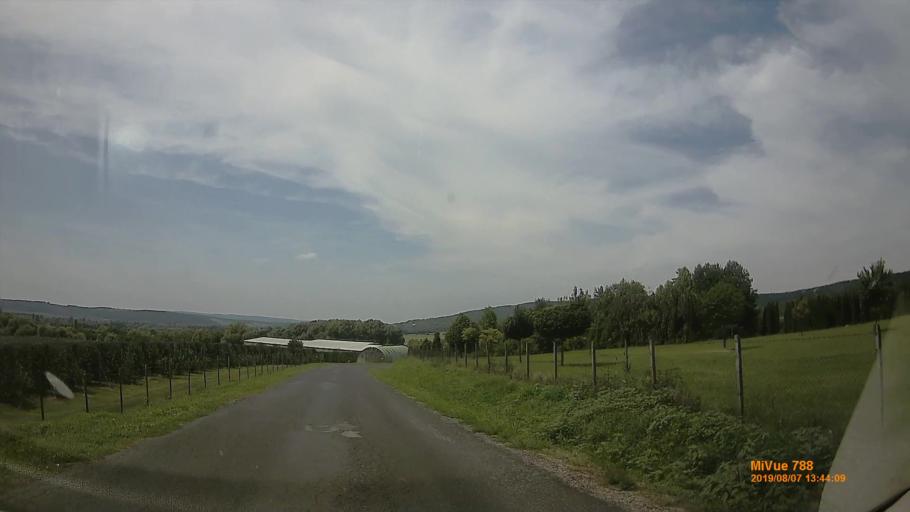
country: HU
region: Zala
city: Cserszegtomaj
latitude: 46.8835
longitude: 17.2174
